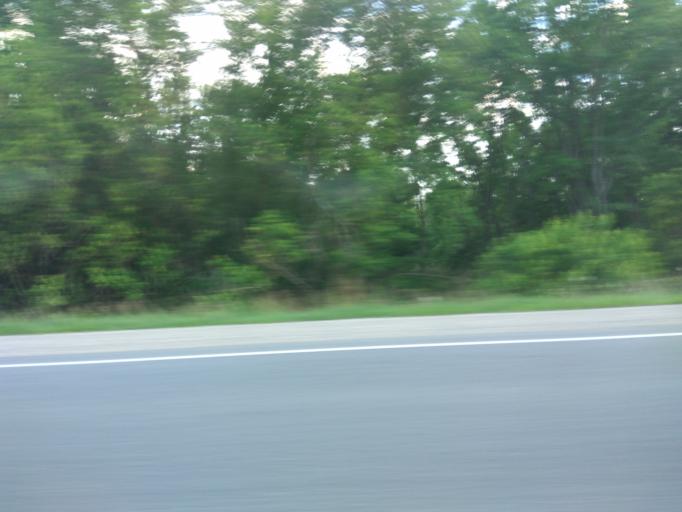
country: CA
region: Ontario
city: Stratford
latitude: 43.3693
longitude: -80.8022
